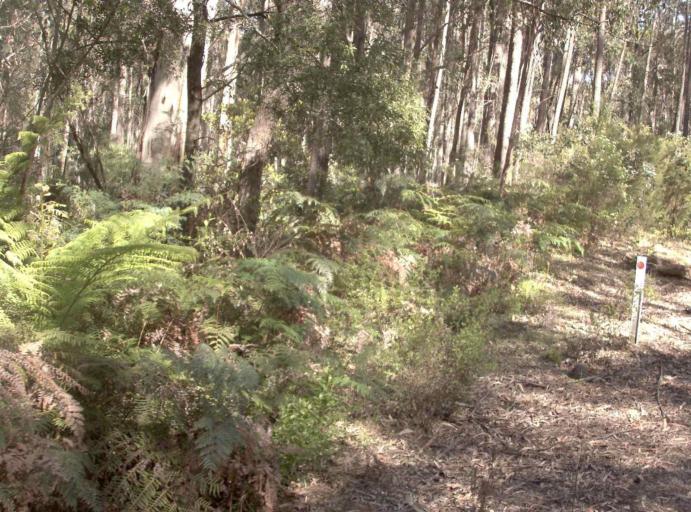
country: AU
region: New South Wales
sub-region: Bombala
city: Bombala
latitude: -37.2823
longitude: 148.7174
